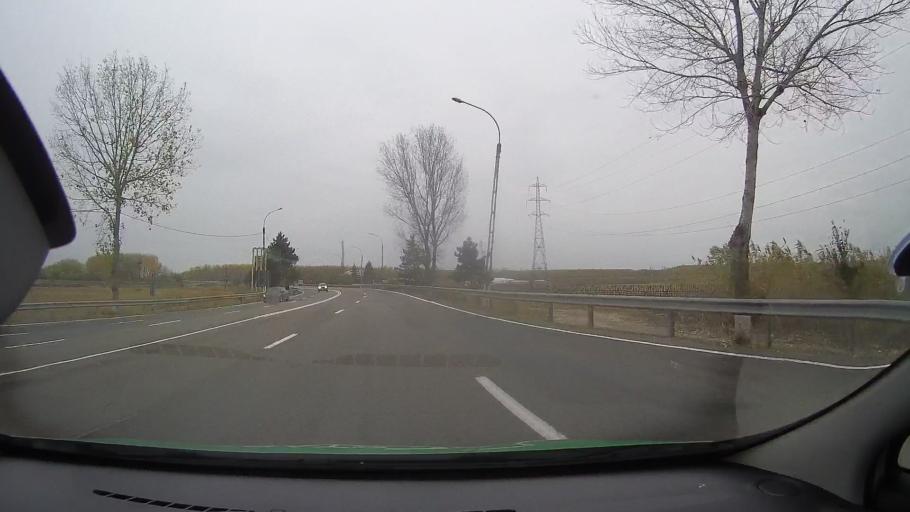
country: RO
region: Ialomita
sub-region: Comuna Giurgeni
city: Giurgeni
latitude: 44.7499
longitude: 27.8926
